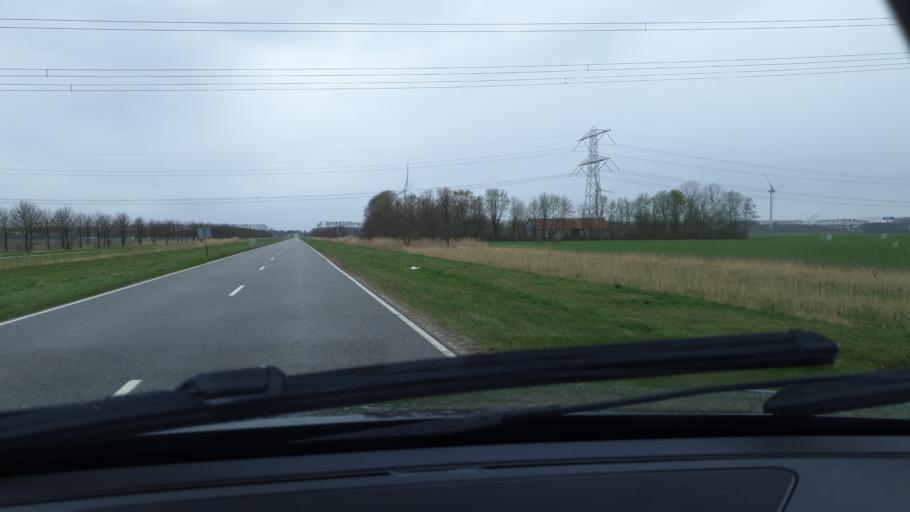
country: NL
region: Flevoland
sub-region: Gemeente Lelystad
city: Lelystad
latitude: 52.5206
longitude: 5.5522
